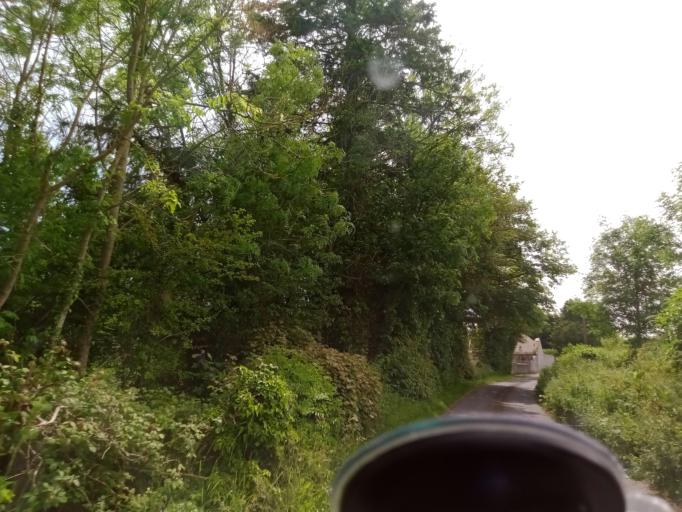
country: IE
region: Leinster
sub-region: Kilkenny
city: Thomastown
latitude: 52.5630
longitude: -7.1023
